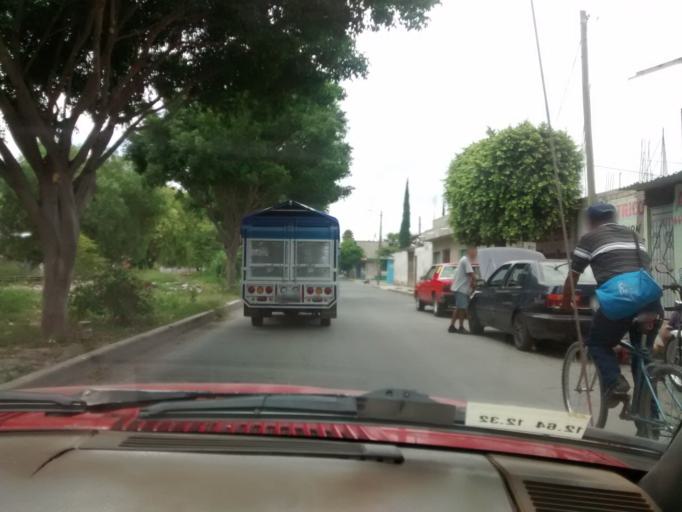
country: MX
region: Puebla
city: Tehuacan
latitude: 18.4714
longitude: -97.4058
